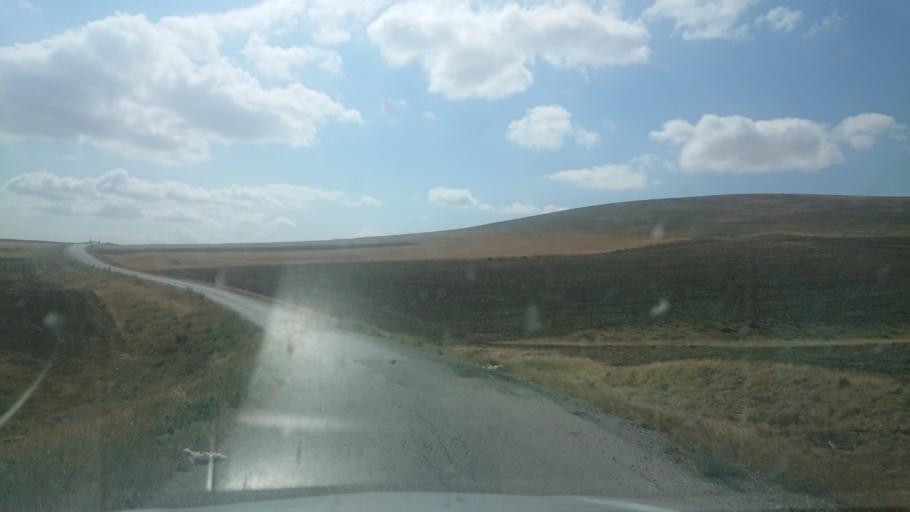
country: TR
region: Aksaray
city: Sariyahsi
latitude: 39.0030
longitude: 33.9644
